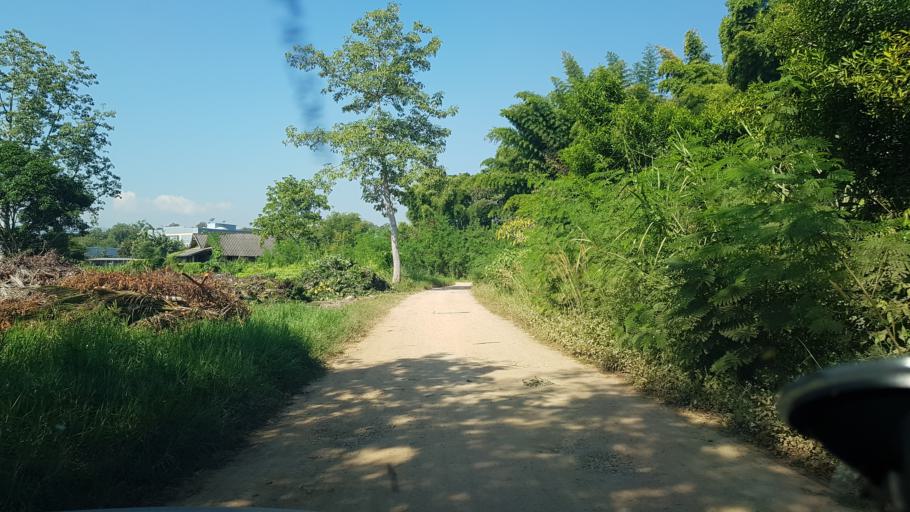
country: TH
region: Chiang Rai
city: Chiang Rai
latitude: 19.9017
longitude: 99.7948
